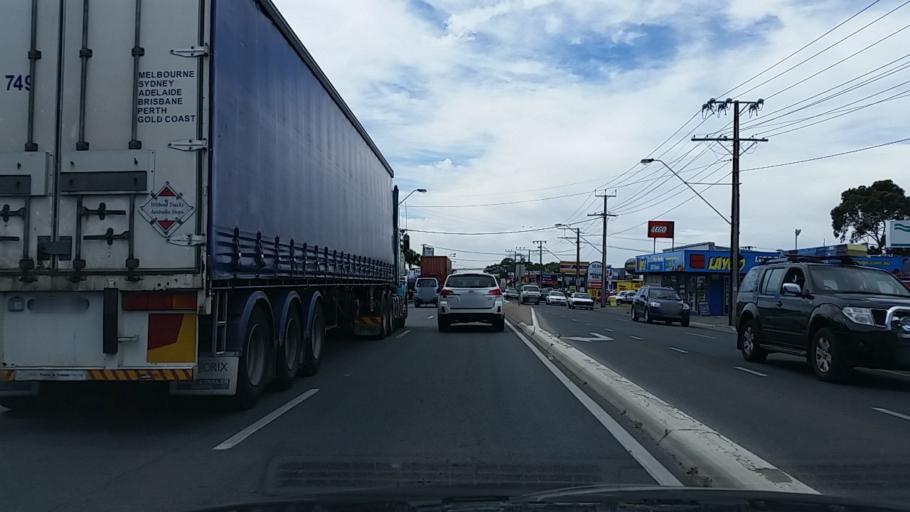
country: AU
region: South Australia
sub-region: Marion
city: Clovelly Park
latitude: -35.0019
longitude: 138.5755
